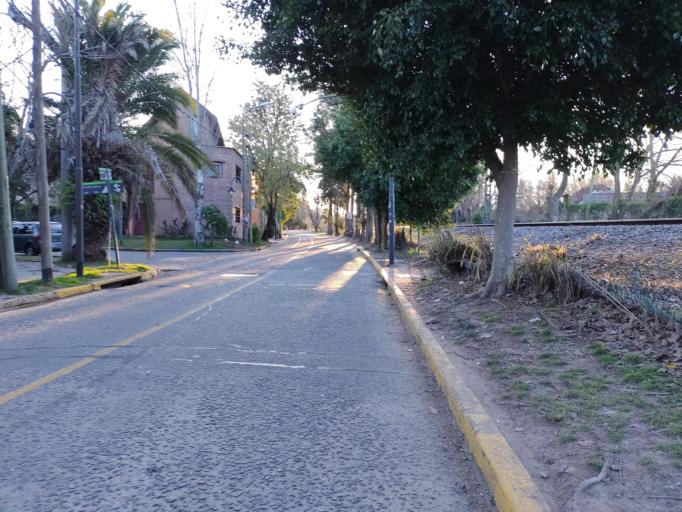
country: AR
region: Buenos Aires
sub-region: Partido de San Isidro
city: San Isidro
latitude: -34.4457
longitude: -58.5335
